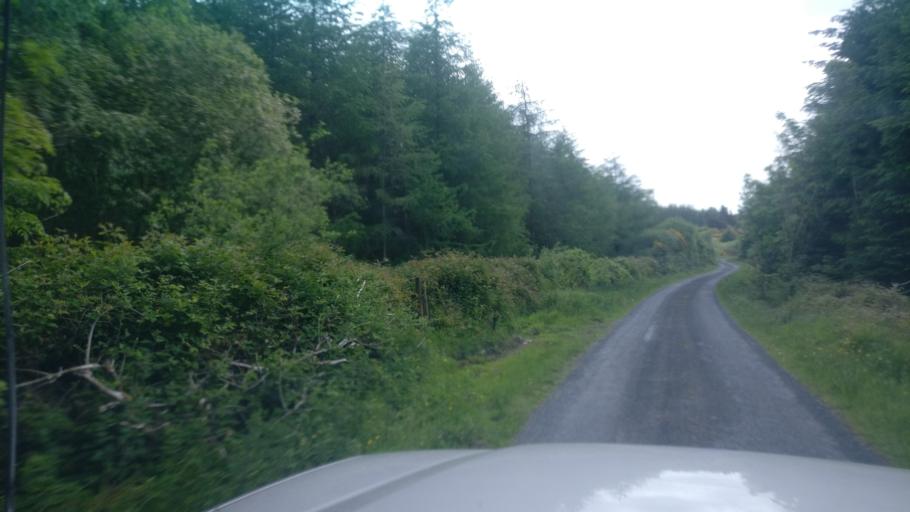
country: IE
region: Connaught
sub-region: County Galway
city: Gort
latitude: 53.1196
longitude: -8.6900
